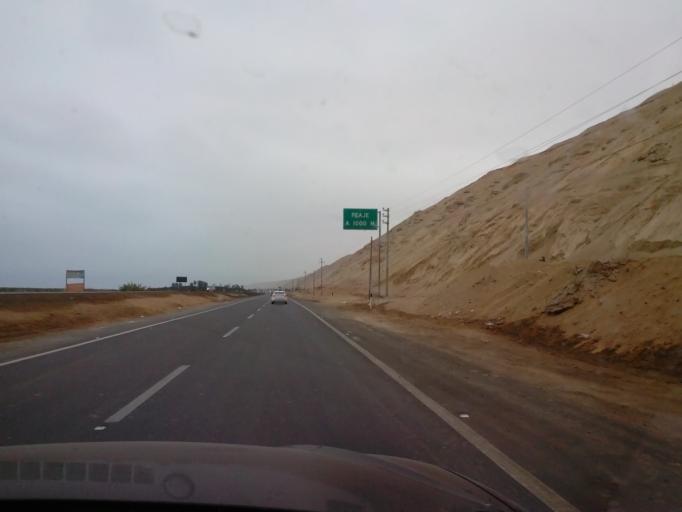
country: PE
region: Ica
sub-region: Provincia de Chincha
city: San Pedro
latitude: -13.3962
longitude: -76.1972
